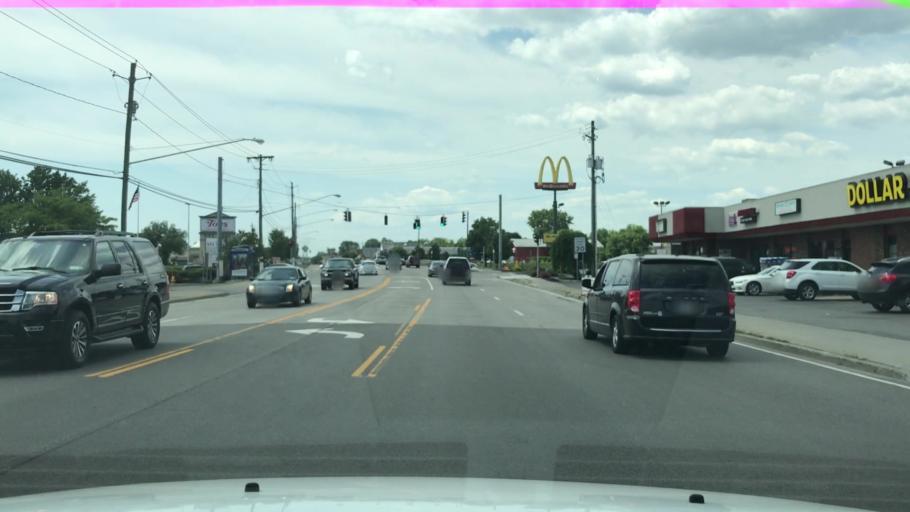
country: US
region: New York
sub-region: Erie County
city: Depew
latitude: 42.9012
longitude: -78.6828
